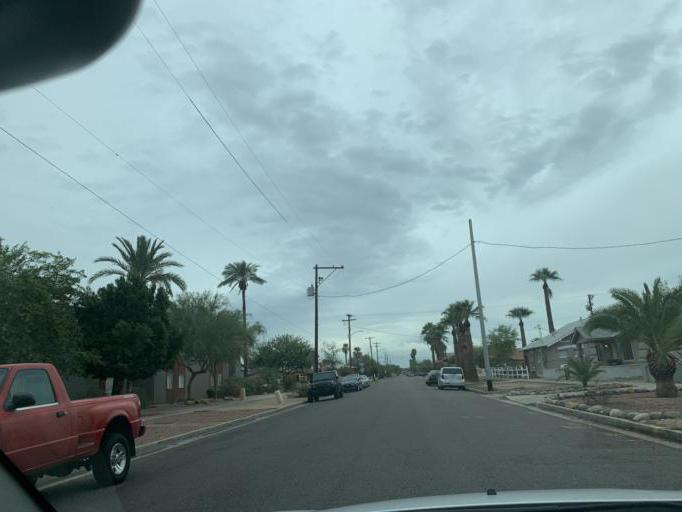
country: US
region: Arizona
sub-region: Maricopa County
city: Phoenix
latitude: 33.4599
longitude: -112.0630
